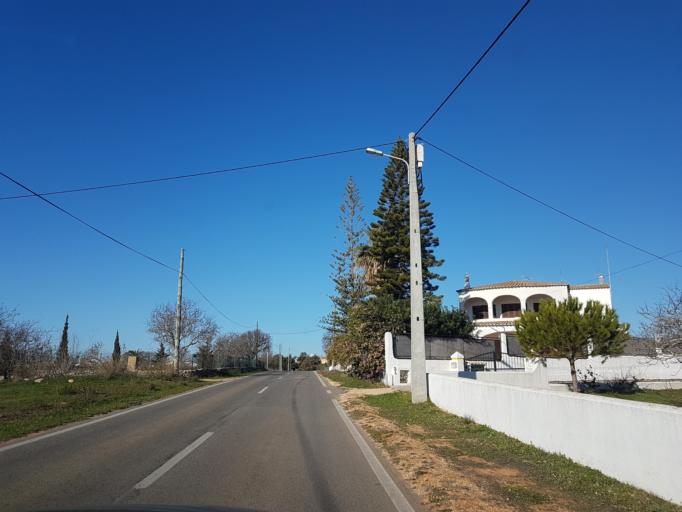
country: PT
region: Faro
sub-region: Lagoa
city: Carvoeiro
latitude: 37.0935
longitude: -8.4323
